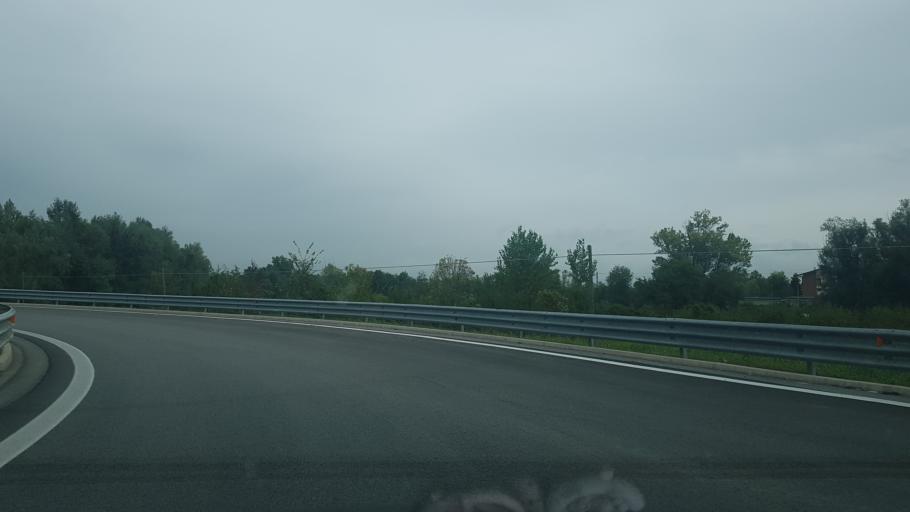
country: IT
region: Piedmont
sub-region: Provincia di Cuneo
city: Breo
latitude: 44.4089
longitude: 7.8042
